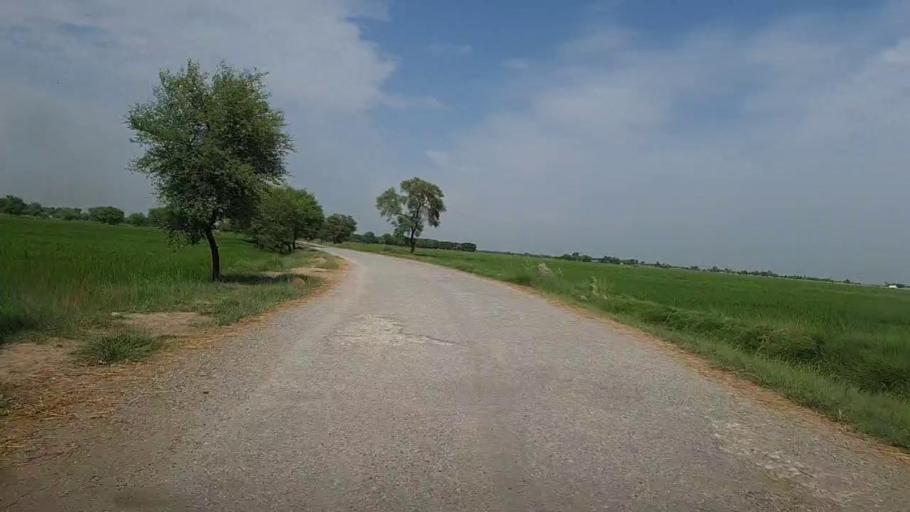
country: PK
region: Sindh
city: Thul
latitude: 28.2328
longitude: 68.7966
